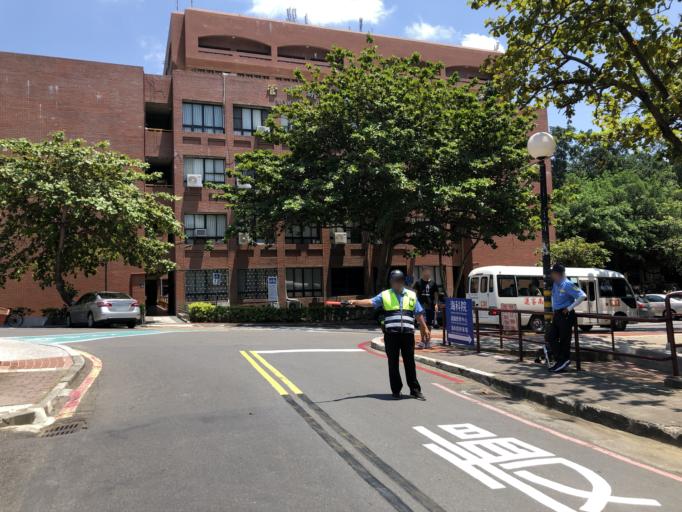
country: TW
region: Kaohsiung
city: Kaohsiung
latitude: 22.6277
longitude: 120.2648
